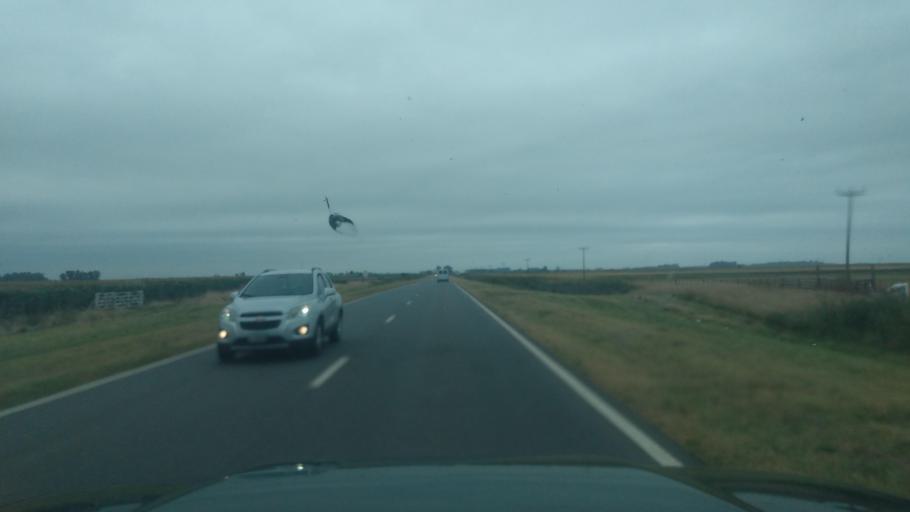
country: AR
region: Buenos Aires
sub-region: Partido de Nueve de Julio
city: Nueve de Julio
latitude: -35.3802
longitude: -60.7259
